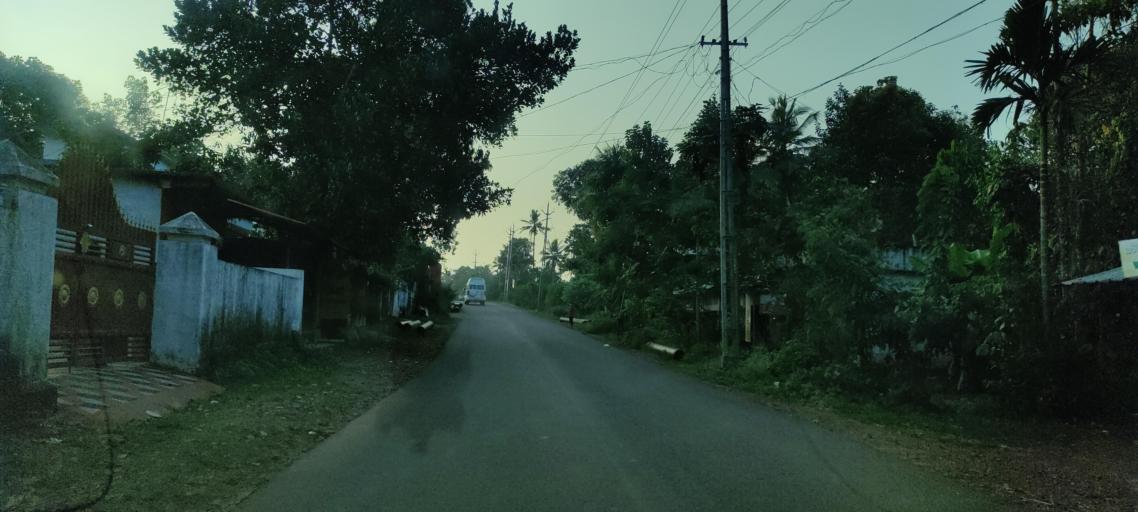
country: IN
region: Kerala
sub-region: Alappuzha
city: Kattanam
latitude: 9.1505
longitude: 76.5817
